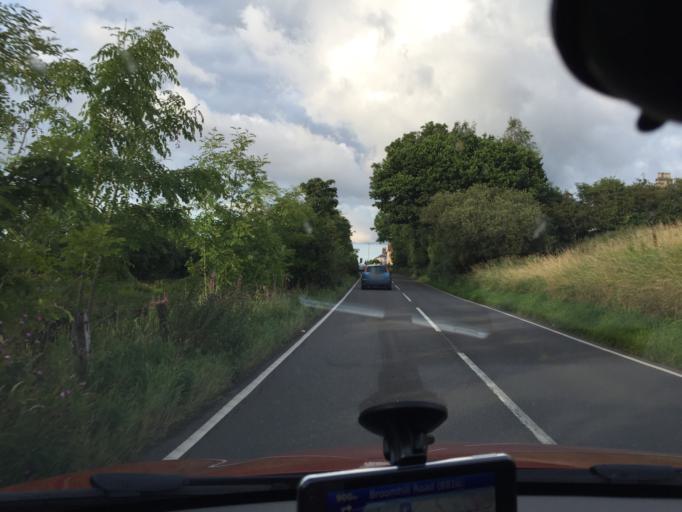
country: GB
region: Scotland
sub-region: Falkirk
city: Bonnybridge
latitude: 55.9939
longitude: -3.8982
